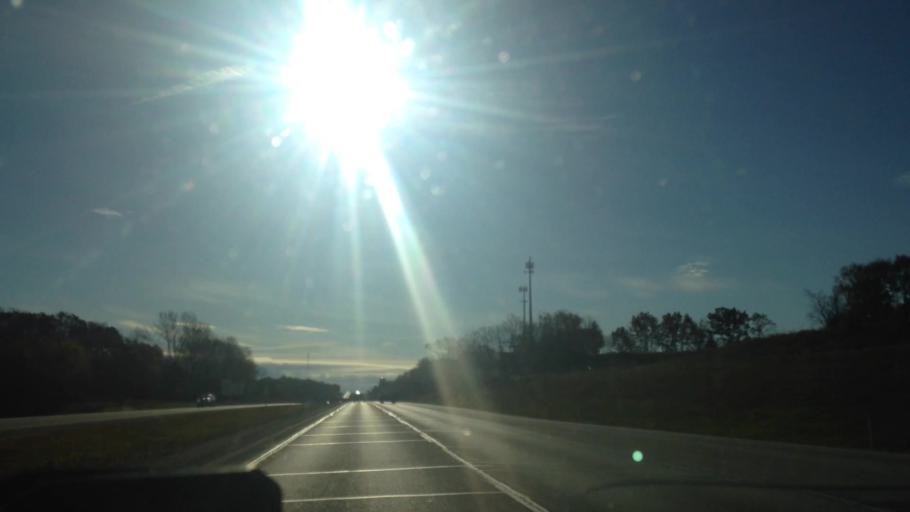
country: US
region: Wisconsin
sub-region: Washington County
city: Slinger
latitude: 43.3449
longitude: -88.2792
